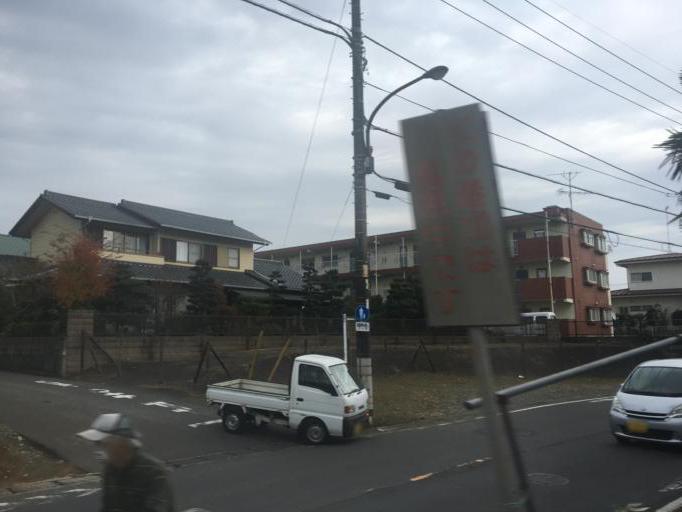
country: JP
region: Tokyo
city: Fussa
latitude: 35.7745
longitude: 139.3465
